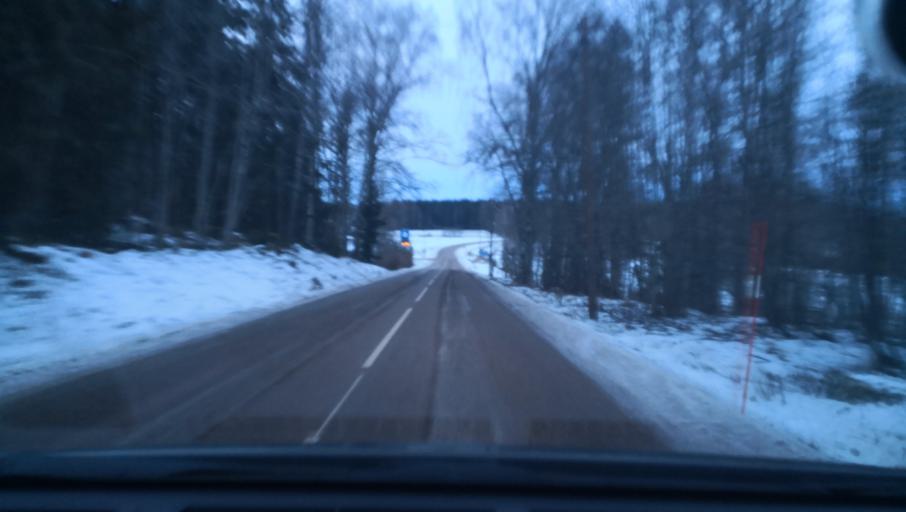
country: SE
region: Dalarna
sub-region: Avesta Kommun
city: Horndal
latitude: 60.1958
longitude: 16.4640
